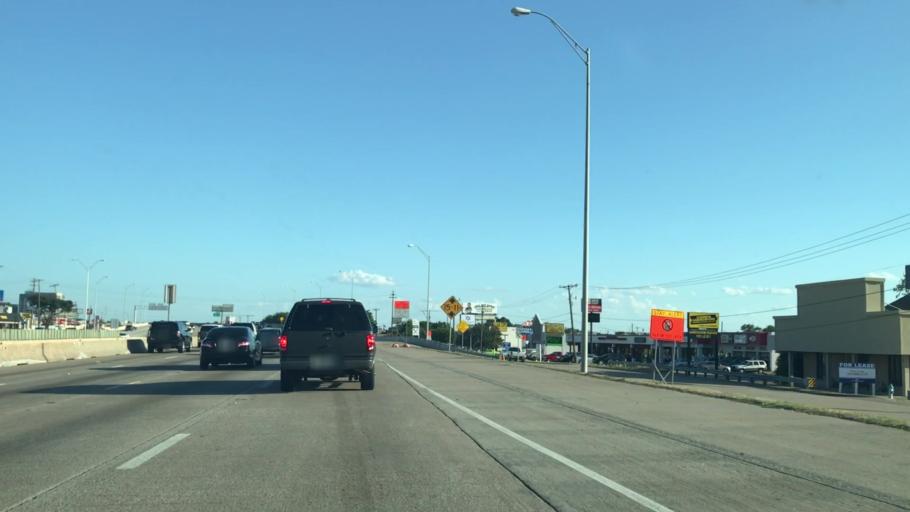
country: US
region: Texas
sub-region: Collin County
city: Plano
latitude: 33.0241
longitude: -96.7102
